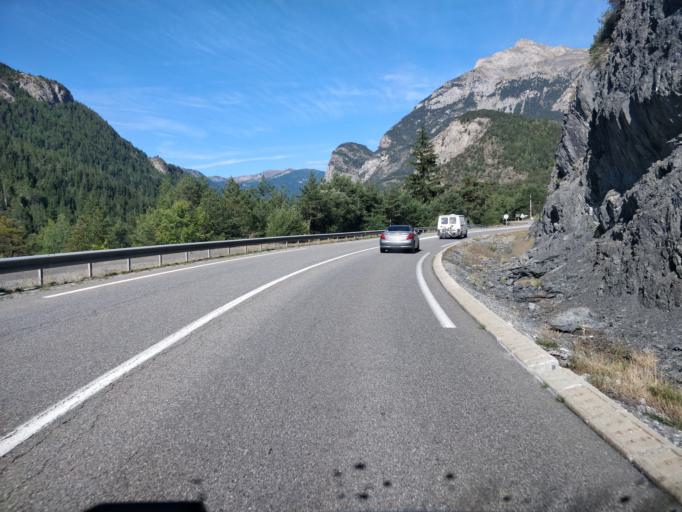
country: FR
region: Provence-Alpes-Cote d'Azur
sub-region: Departement des Alpes-de-Haute-Provence
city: Barcelonnette
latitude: 44.3988
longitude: 6.5342
